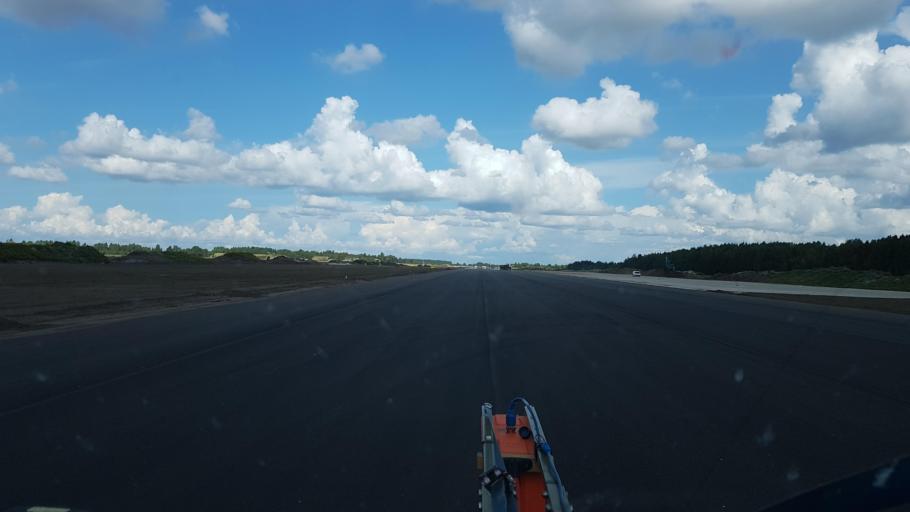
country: EE
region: Paernumaa
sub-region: Sauga vald
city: Sauga
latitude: 58.4159
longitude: 24.4689
